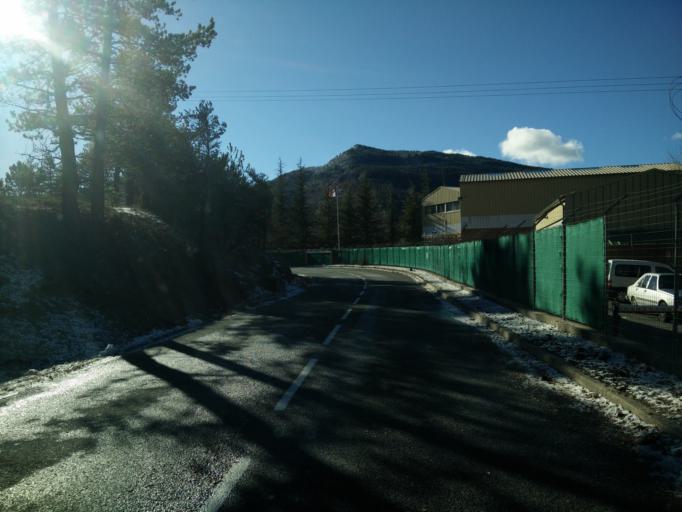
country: FR
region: Provence-Alpes-Cote d'Azur
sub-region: Departement des Alpes-de-Haute-Provence
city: Castellane
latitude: 43.8831
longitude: 6.5405
